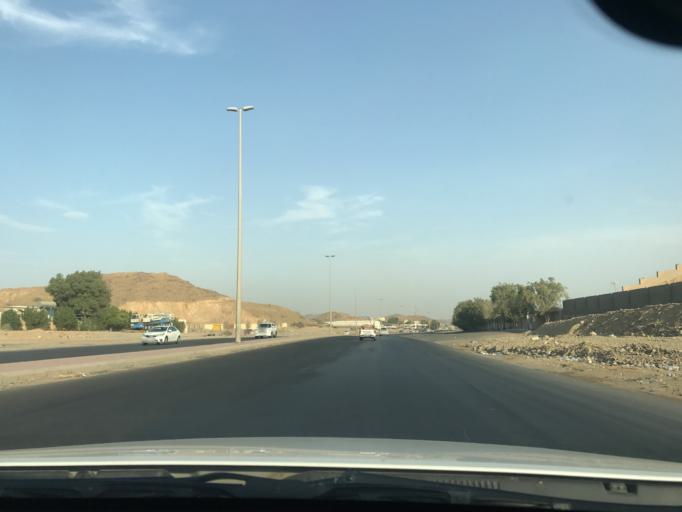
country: SA
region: Makkah
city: Jeddah
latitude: 21.4103
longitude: 39.4238
